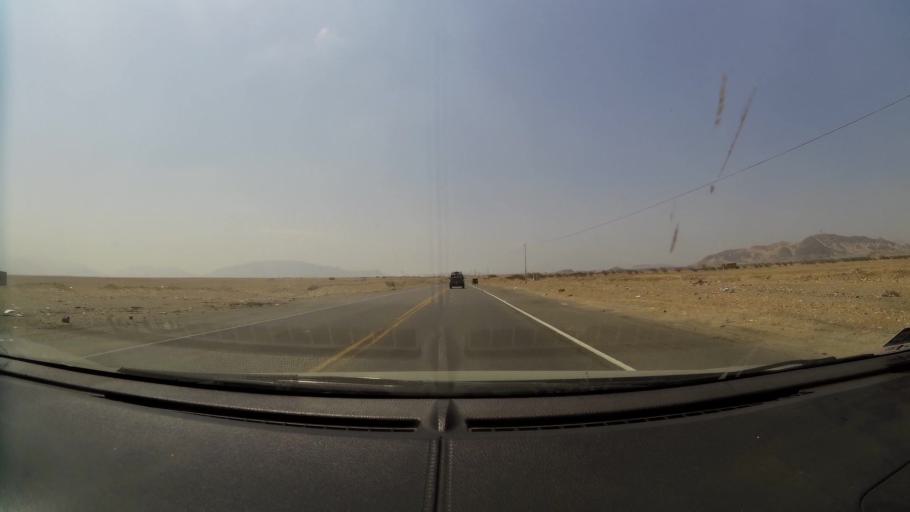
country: PE
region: La Libertad
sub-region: Provincia de Pacasmayo
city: Pacasmayo
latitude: -7.3686
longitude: -79.5329
